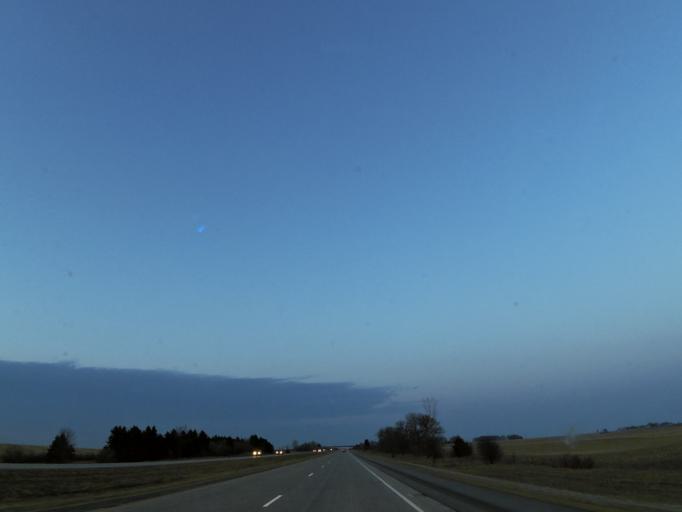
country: US
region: Minnesota
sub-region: Mower County
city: Grand Meadow
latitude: 43.7681
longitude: -92.6336
